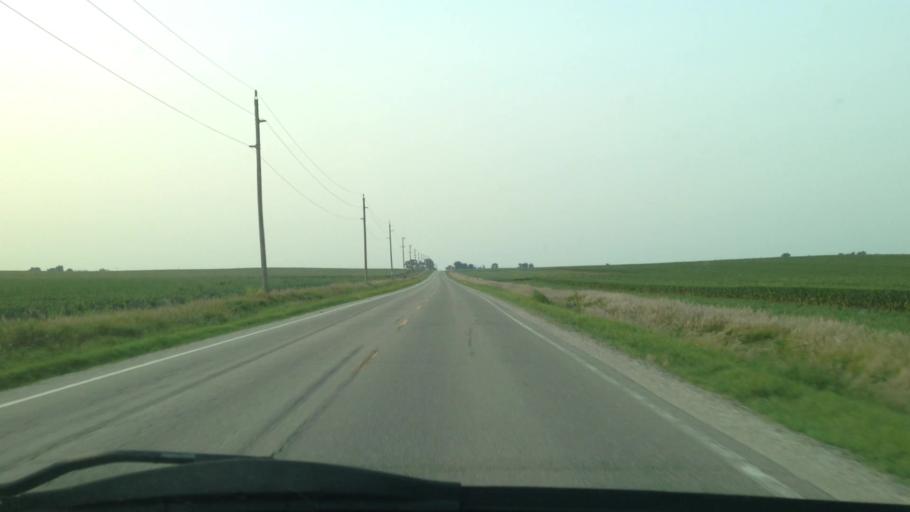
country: US
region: Iowa
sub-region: Iowa County
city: Marengo
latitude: 41.9498
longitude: -92.0852
